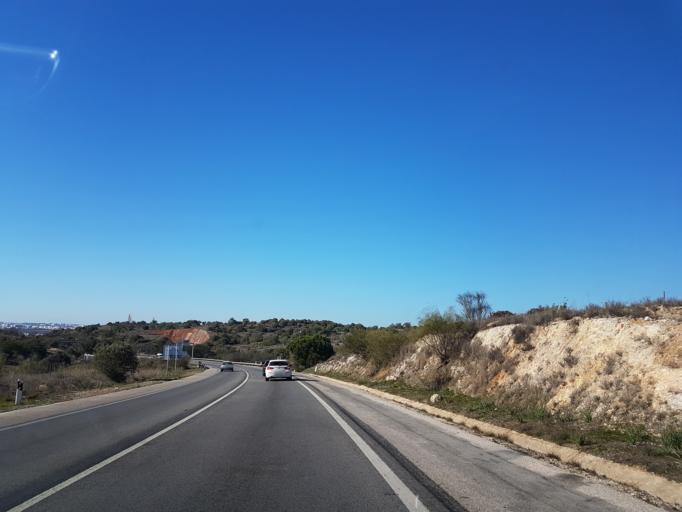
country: PT
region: Faro
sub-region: Lagoa
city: Estombar
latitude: 37.1533
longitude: -8.4897
